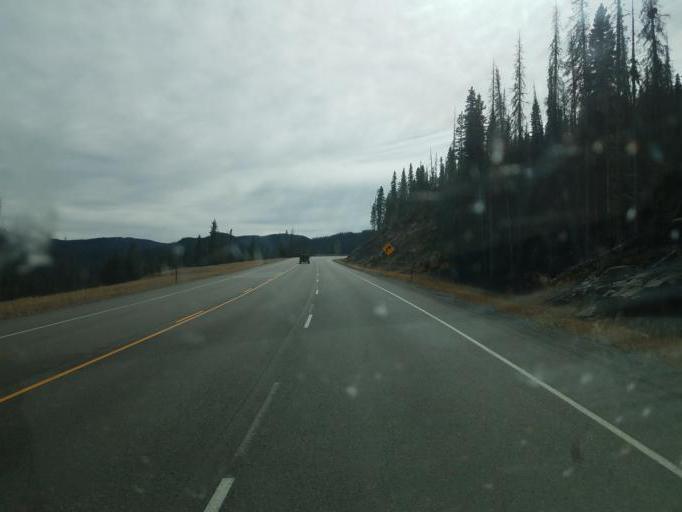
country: US
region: Colorado
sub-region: Archuleta County
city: Pagosa Springs
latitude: 37.4947
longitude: -106.7674
